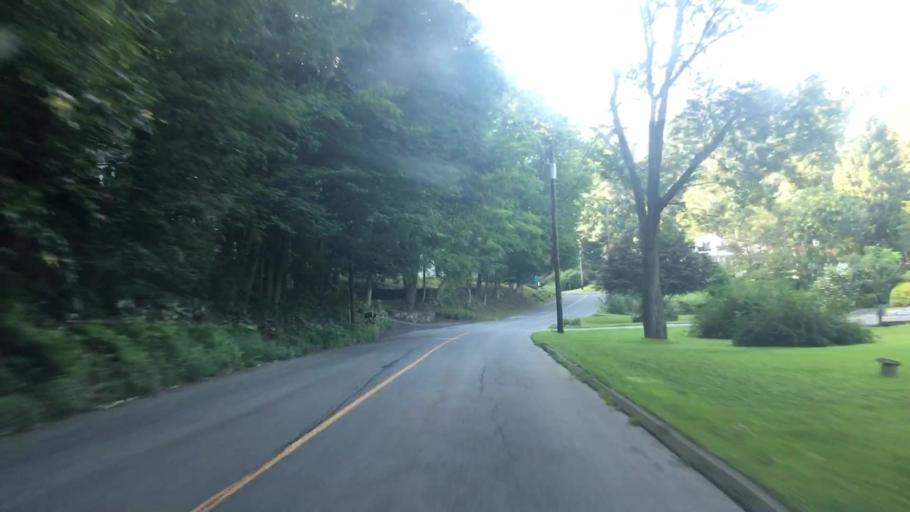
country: US
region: Connecticut
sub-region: Middlesex County
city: Deep River Center
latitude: 41.3903
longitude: -72.4461
